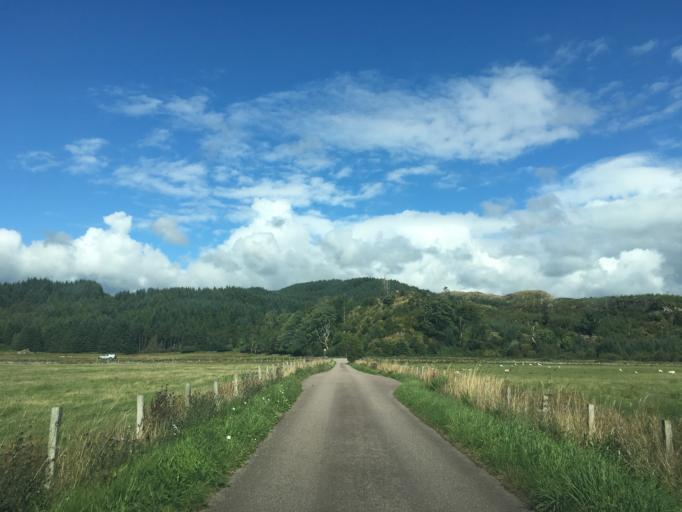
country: GB
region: Scotland
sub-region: Argyll and Bute
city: Lochgilphead
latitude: 56.0874
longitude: -5.4709
